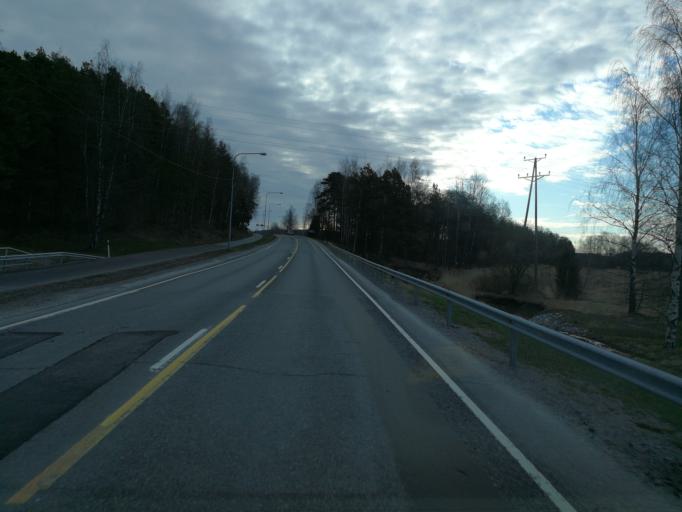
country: FI
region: Varsinais-Suomi
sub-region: Turku
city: Piikkioe
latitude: 60.4202
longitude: 22.4920
